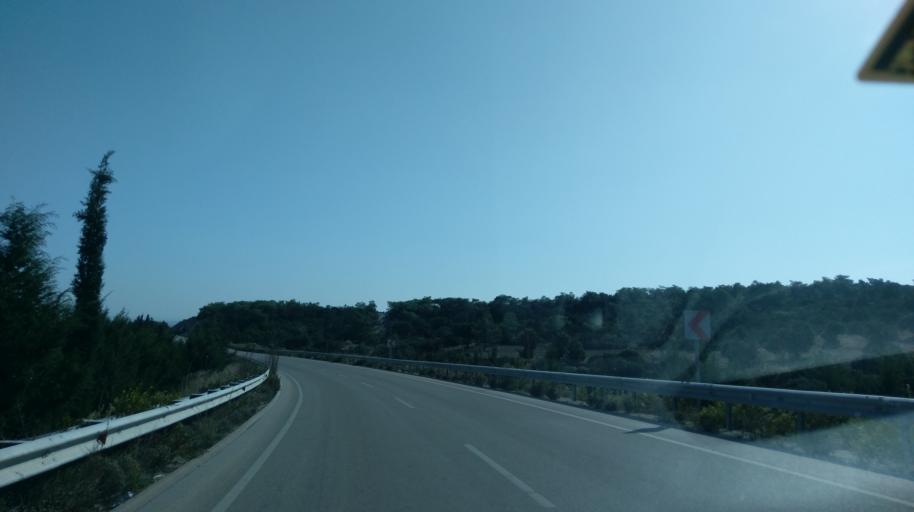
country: CY
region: Ammochostos
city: Trikomo
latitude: 35.4192
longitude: 33.9806
